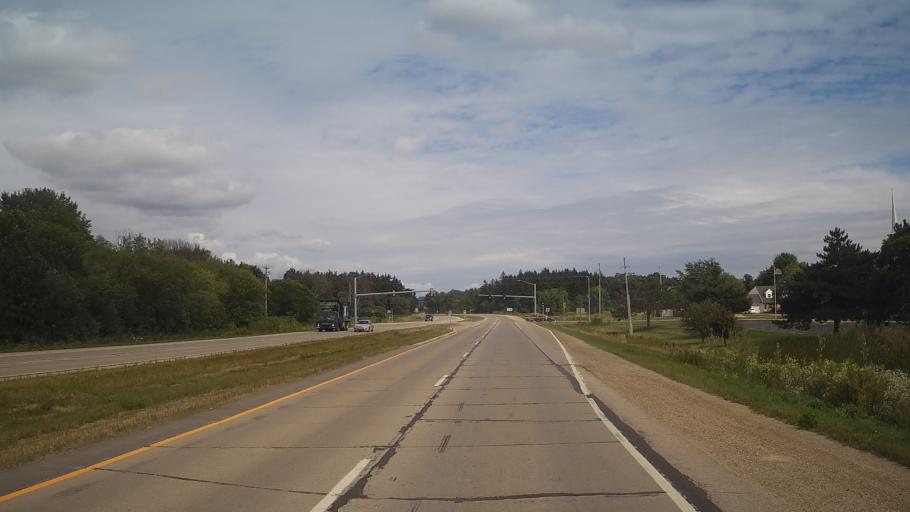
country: US
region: Wisconsin
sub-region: Winnebago County
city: Oshkosh
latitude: 44.0285
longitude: -88.6052
